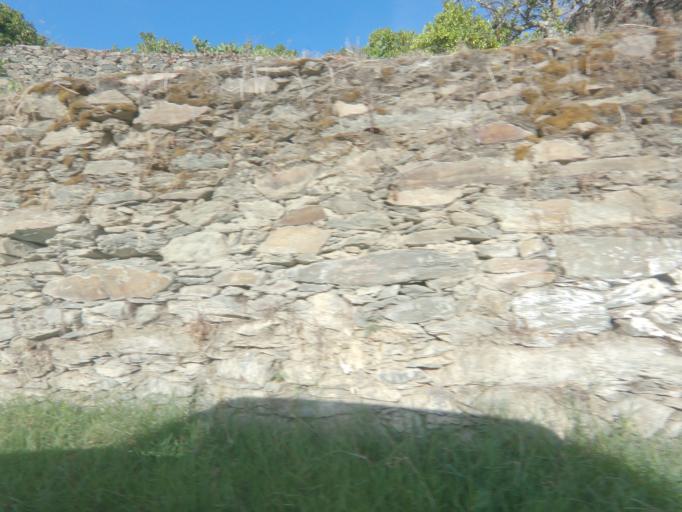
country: PT
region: Vila Real
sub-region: Sabrosa
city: Vilela
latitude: 41.2058
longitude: -7.5386
